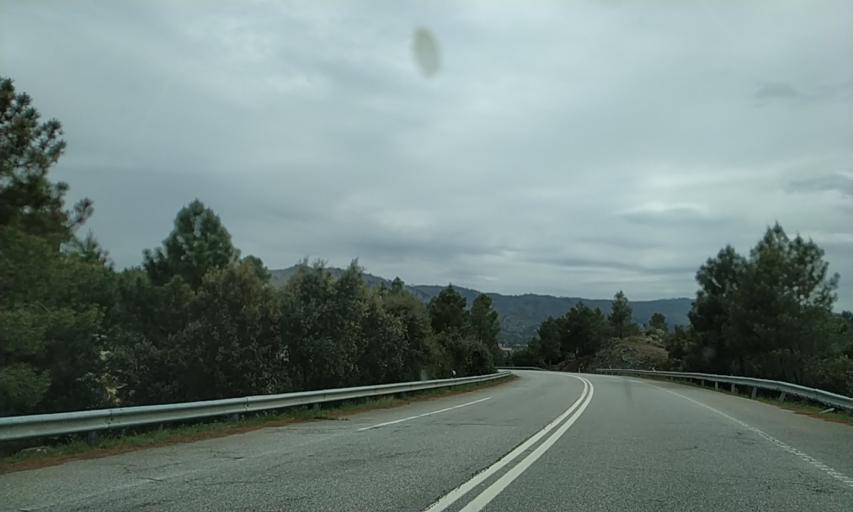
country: PT
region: Guarda
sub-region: Celorico da Beira
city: Celorico da Beira
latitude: 40.6251
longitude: -7.3067
